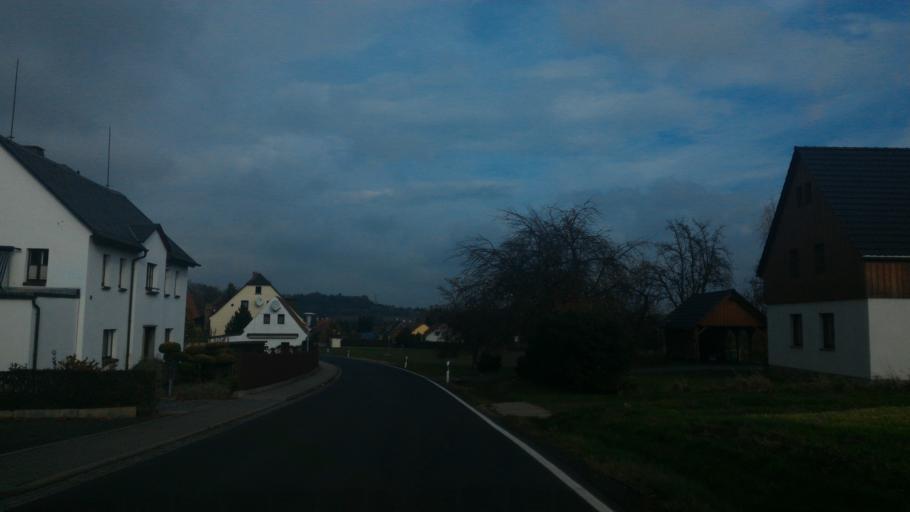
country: DE
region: Saxony
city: Bertsdorf-Hoernitz
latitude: 50.8953
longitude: 14.7517
